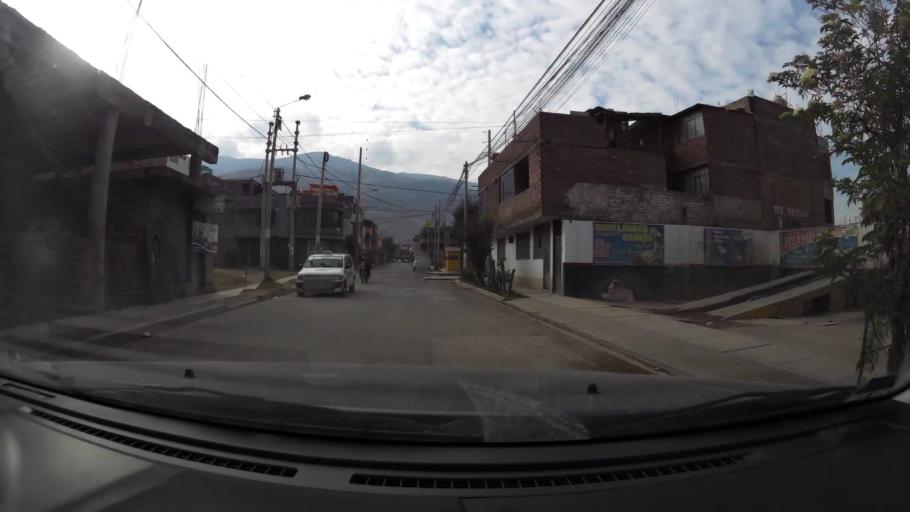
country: PE
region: Junin
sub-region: Provincia de Huancayo
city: Huancayo
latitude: -12.0481
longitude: -75.1952
